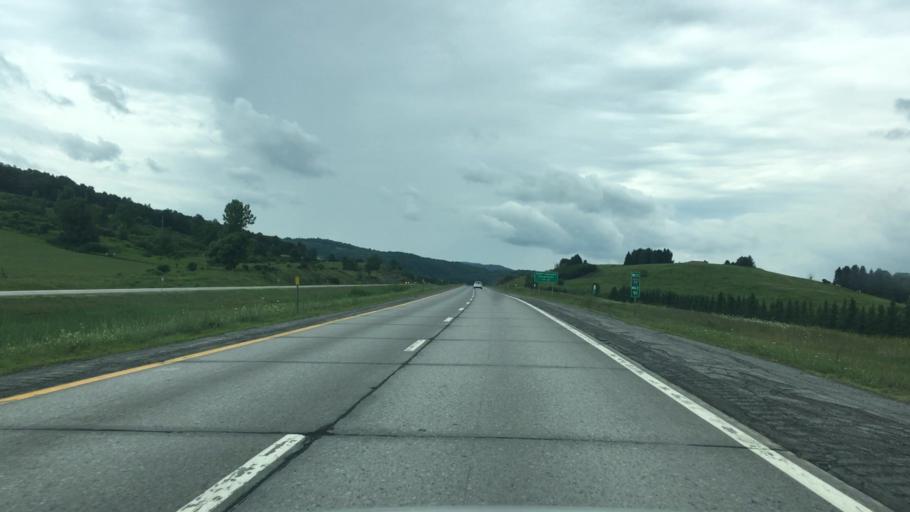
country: US
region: New York
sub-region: Schoharie County
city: Cobleskill
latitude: 42.6669
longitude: -74.4909
